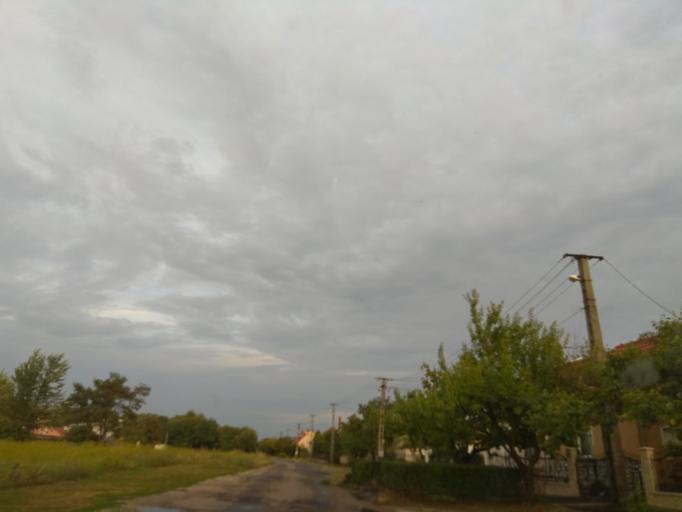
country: HU
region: Borsod-Abauj-Zemplen
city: Miskolc
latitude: 48.0623
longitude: 20.7891
